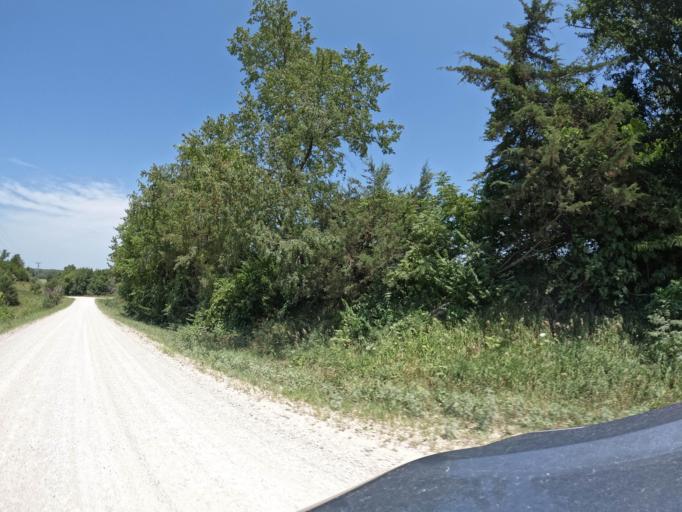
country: US
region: Iowa
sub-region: Henry County
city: Mount Pleasant
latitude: 40.9637
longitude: -91.6726
